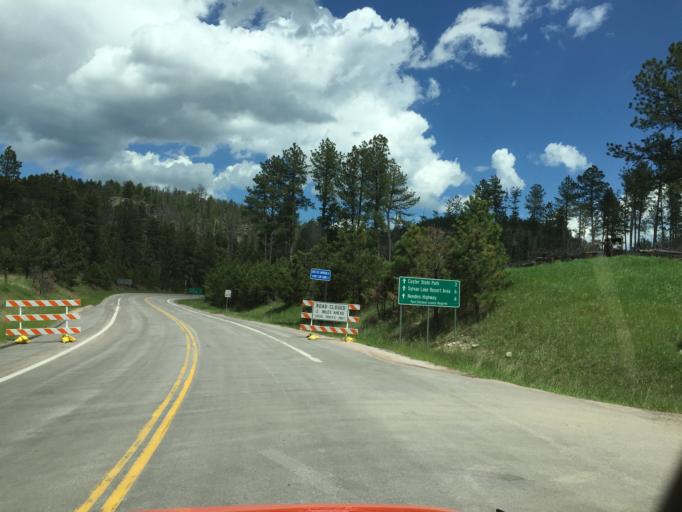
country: US
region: South Dakota
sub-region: Custer County
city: Custer
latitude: 43.8891
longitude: -103.5889
